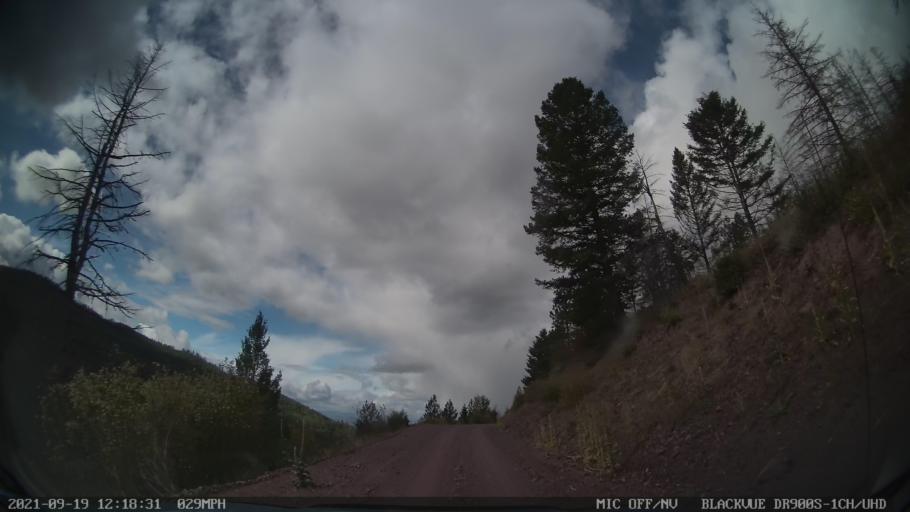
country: US
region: Montana
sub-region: Missoula County
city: Seeley Lake
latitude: 47.1761
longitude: -113.3653
